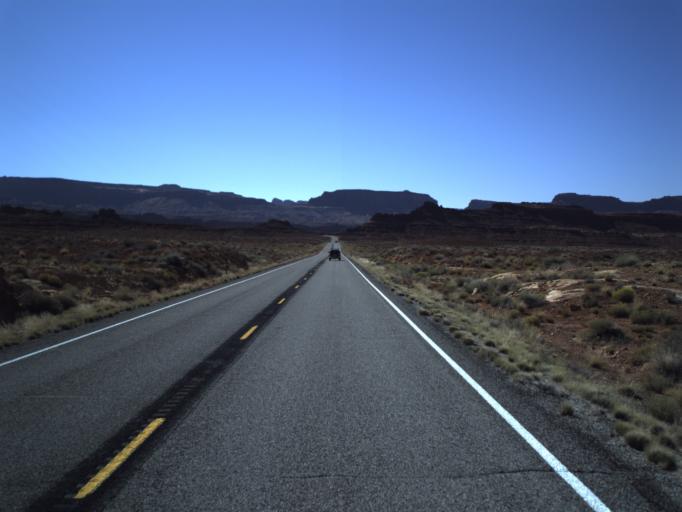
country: US
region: Utah
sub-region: San Juan County
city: Blanding
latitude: 37.8427
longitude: -110.3556
